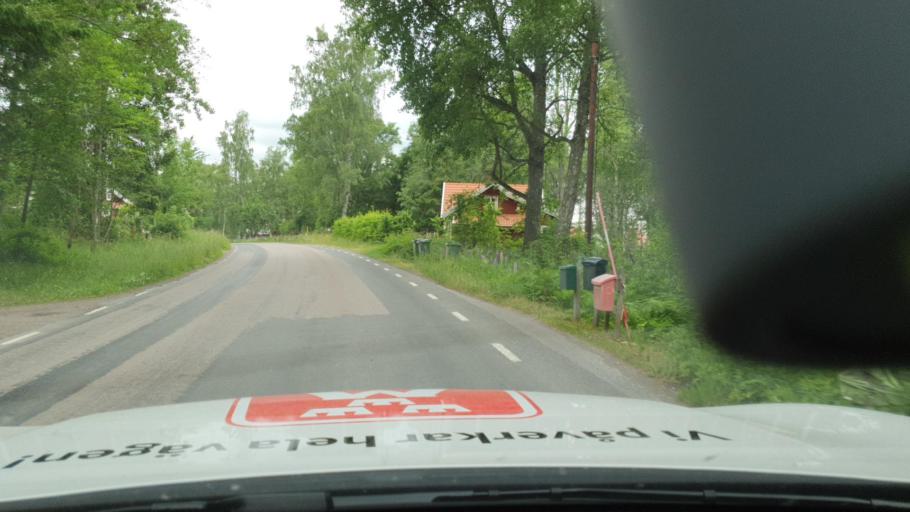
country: SE
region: Vaestra Goetaland
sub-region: Tidaholms Kommun
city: Olofstorp
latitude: 58.3284
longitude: 13.9957
